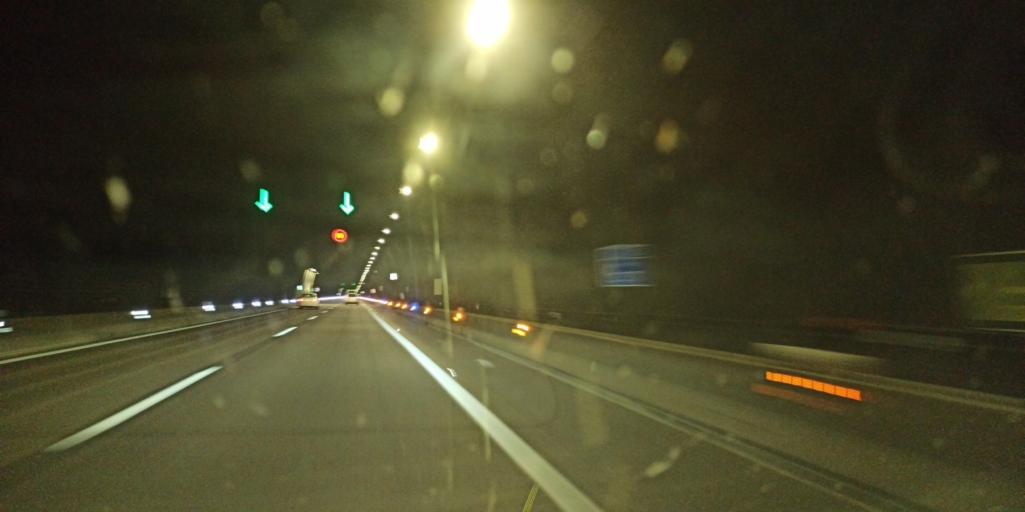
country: ES
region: Catalonia
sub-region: Provincia de Barcelona
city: Sitges
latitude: 41.2494
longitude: 1.8824
